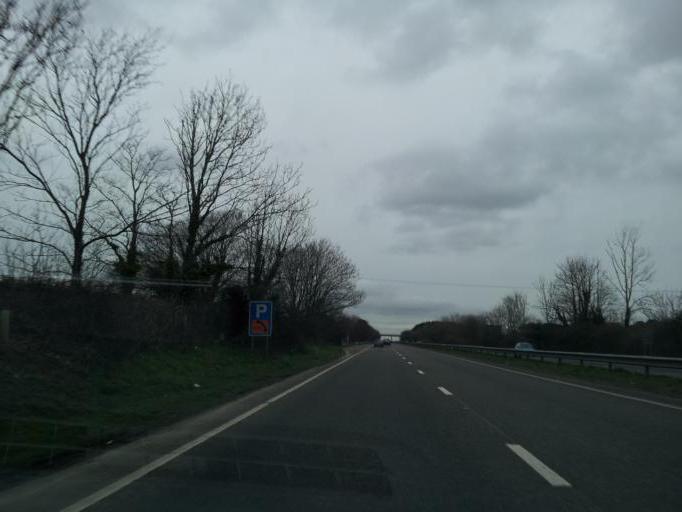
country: GB
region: England
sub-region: Cornwall
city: Redruth
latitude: 50.2497
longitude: -5.2200
